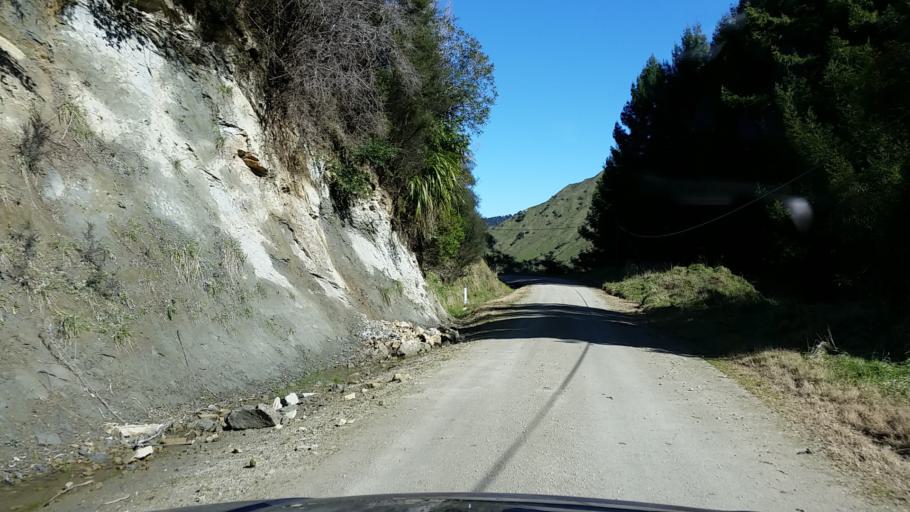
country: NZ
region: Manawatu-Wanganui
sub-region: Wanganui District
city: Wanganui
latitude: -39.5344
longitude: 174.9274
